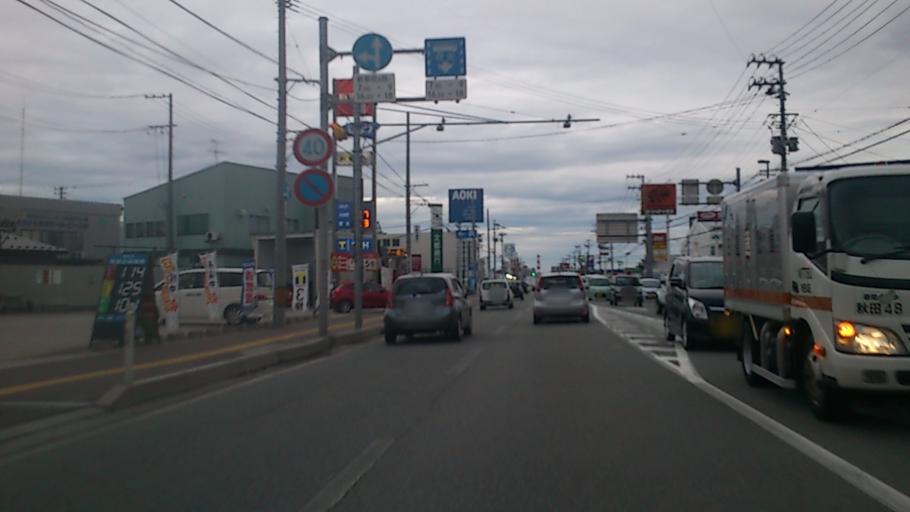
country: JP
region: Akita
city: Akita Shi
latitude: 39.7366
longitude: 140.0982
